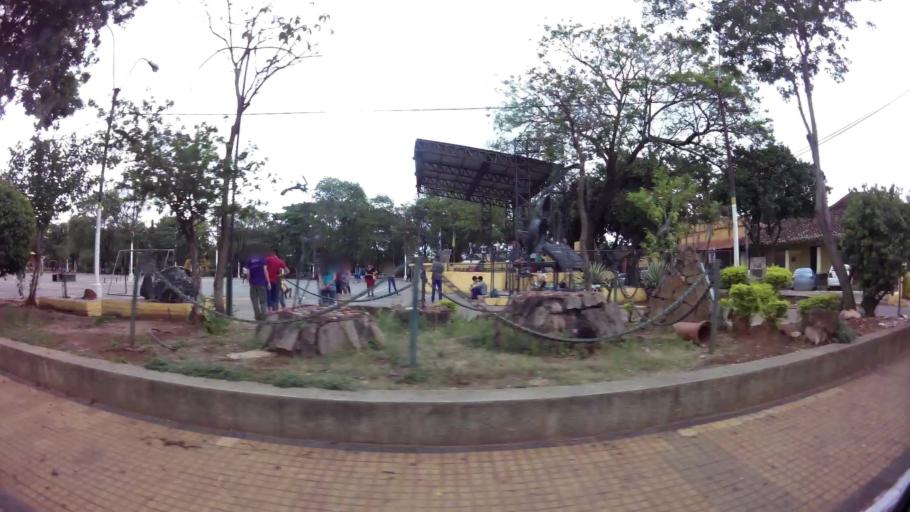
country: PY
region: Central
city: San Lorenzo
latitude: -25.2659
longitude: -57.4931
